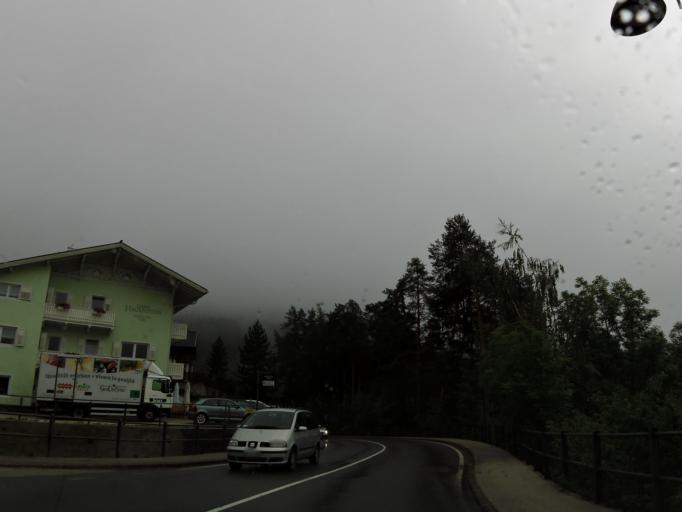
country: IT
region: Trentino-Alto Adige
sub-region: Bolzano
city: Siusi
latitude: 46.5426
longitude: 11.5624
